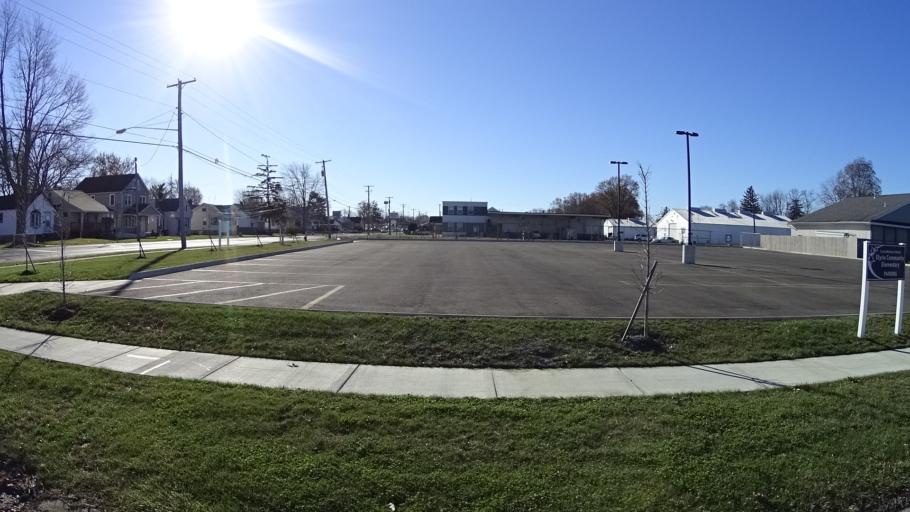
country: US
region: Ohio
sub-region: Lorain County
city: Elyria
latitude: 41.3813
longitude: -82.0779
